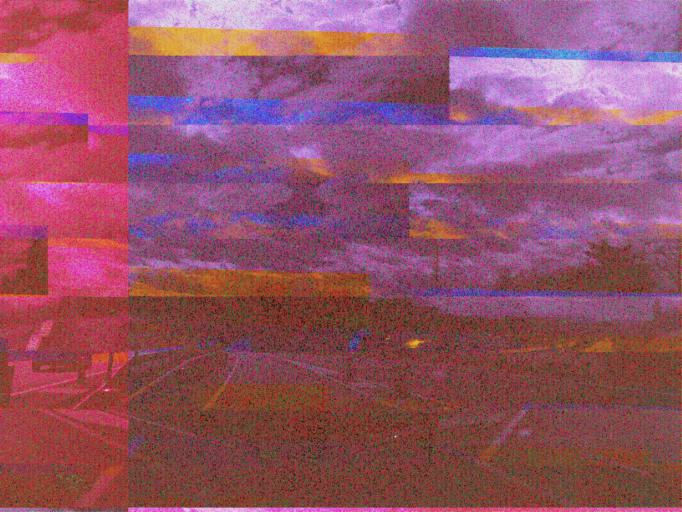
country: ES
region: Madrid
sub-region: Provincia de Madrid
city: Boadilla del Monte
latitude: 40.3974
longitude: -3.8441
